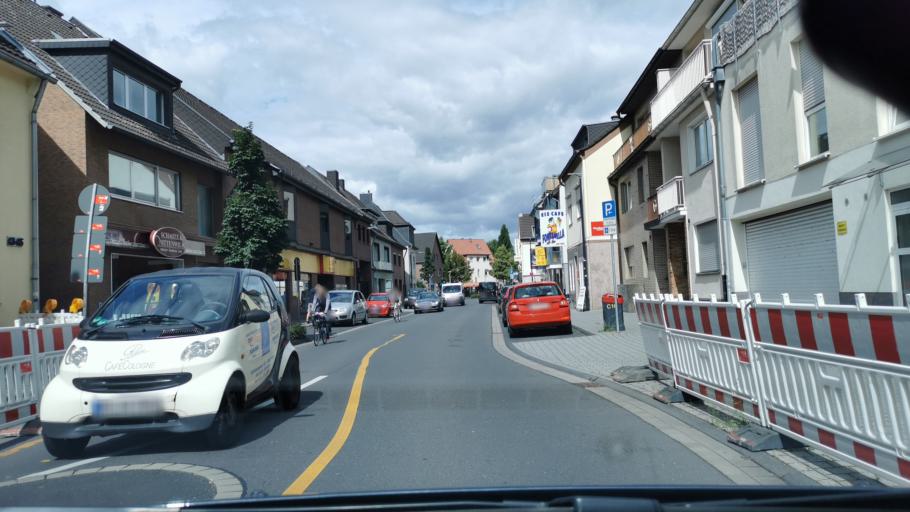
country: DE
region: North Rhine-Westphalia
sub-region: Regierungsbezirk Koln
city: Hurth
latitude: 50.8951
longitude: 6.9016
